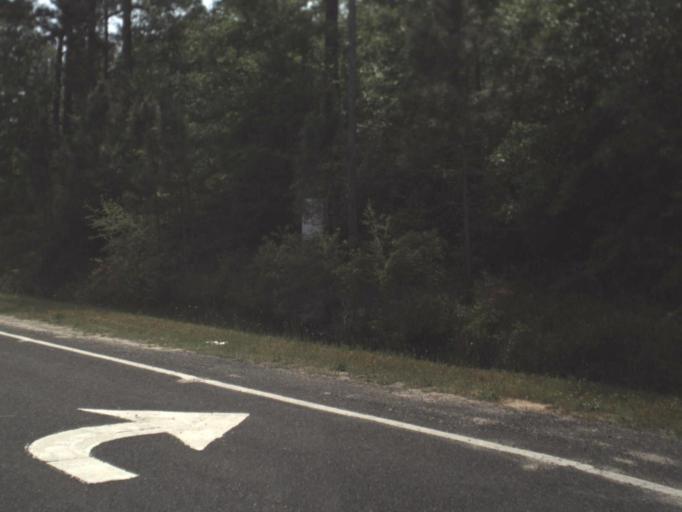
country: US
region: Florida
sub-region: Santa Rosa County
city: Bagdad
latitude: 30.5305
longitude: -87.0874
